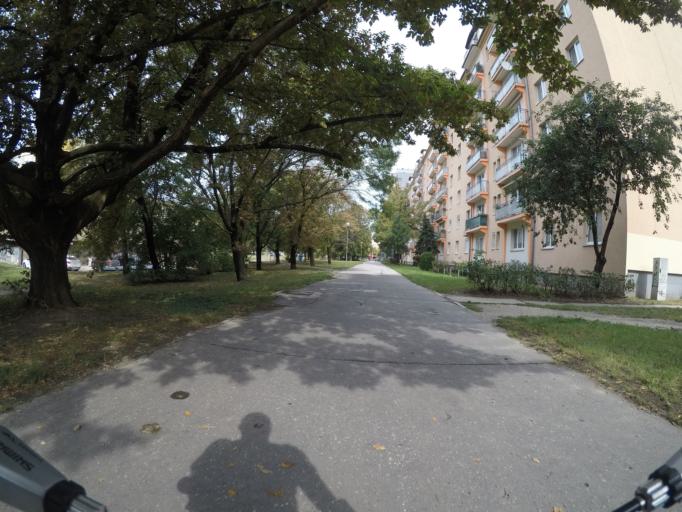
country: SK
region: Bratislavsky
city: Bratislava
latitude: 48.1548
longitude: 17.1564
